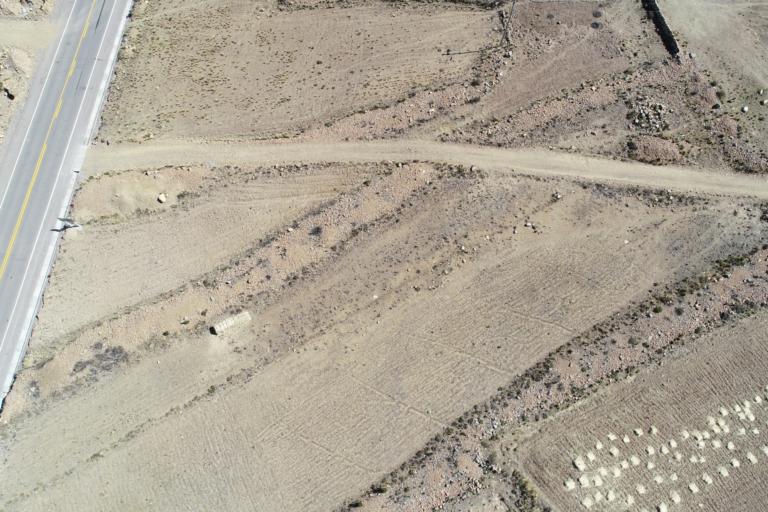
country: BO
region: La Paz
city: Achacachi
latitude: -15.8838
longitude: -68.8122
